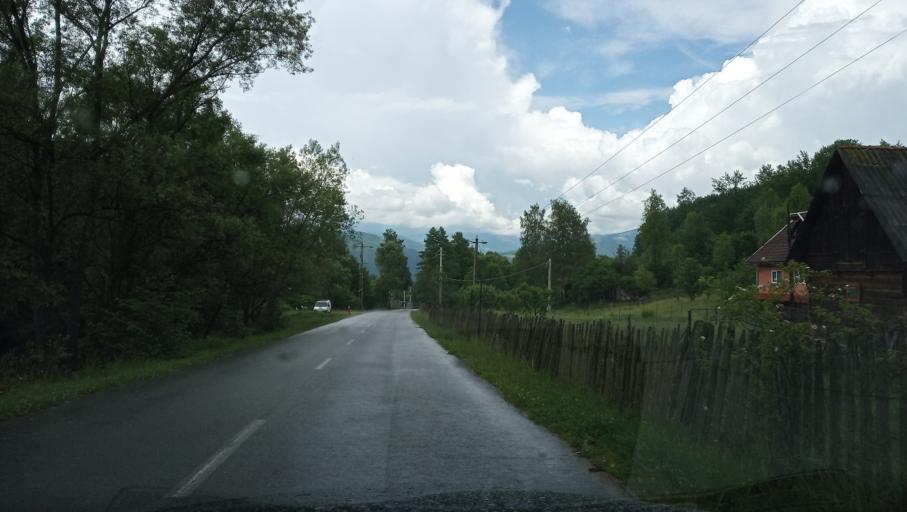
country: RO
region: Hunedoara
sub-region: Oras Petrila
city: Petrila
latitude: 45.4070
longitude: 23.4119
